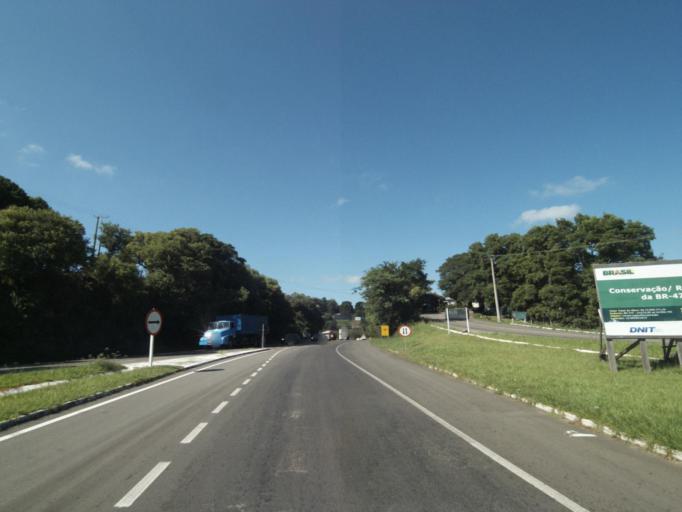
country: BR
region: Rio Grande do Sul
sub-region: Bento Goncalves
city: Bento Goncalves
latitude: -29.1203
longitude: -51.5429
